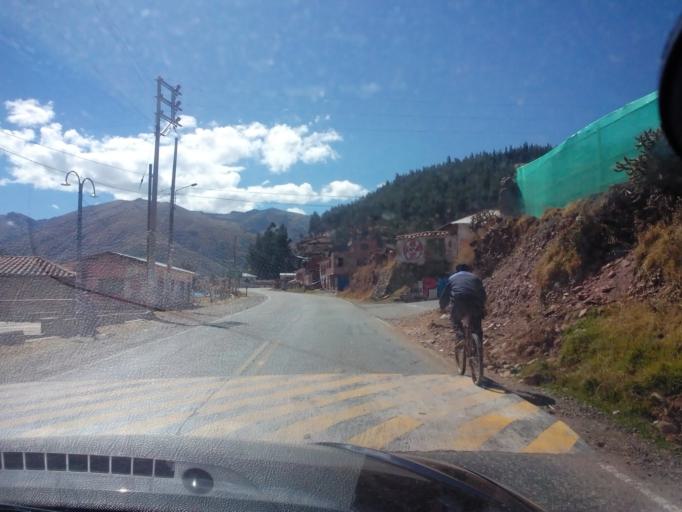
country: PE
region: Cusco
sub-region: Provincia de Canchis
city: Combapata
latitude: -14.0993
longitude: -71.4326
